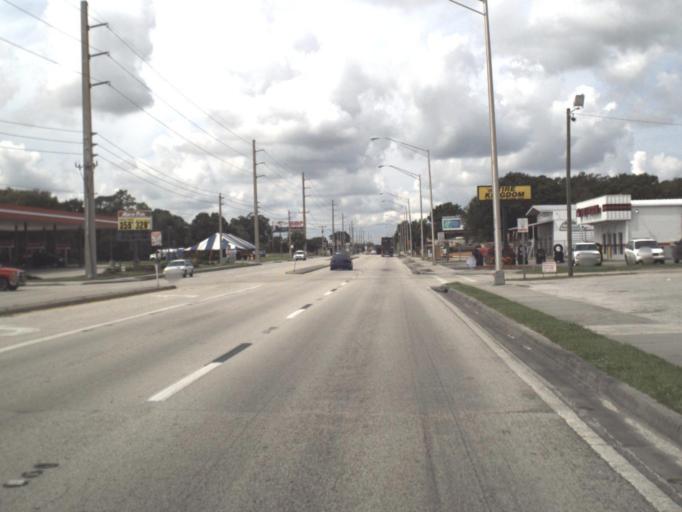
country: US
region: Florida
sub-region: Okeechobee County
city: Cypress Quarters
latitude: 27.2439
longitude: -80.8125
